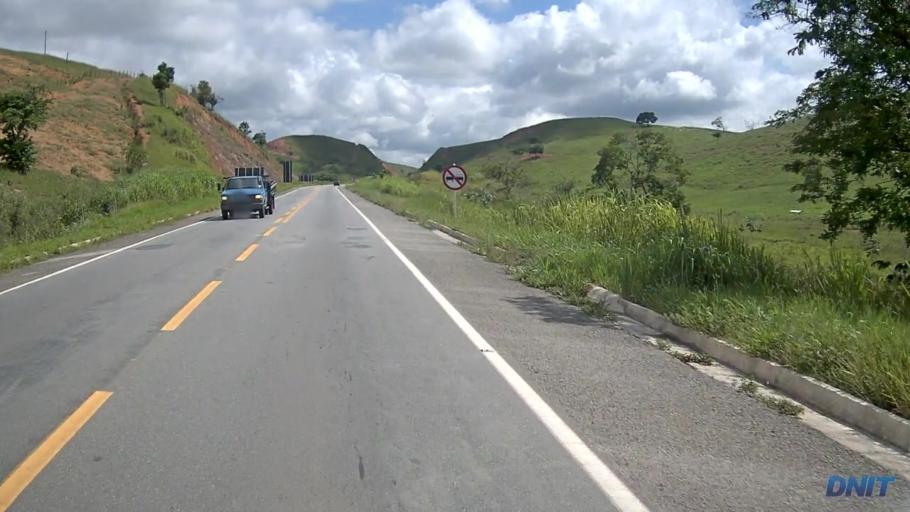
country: BR
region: Minas Gerais
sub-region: Belo Oriente
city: Belo Oriente
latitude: -19.1278
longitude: -42.2135
